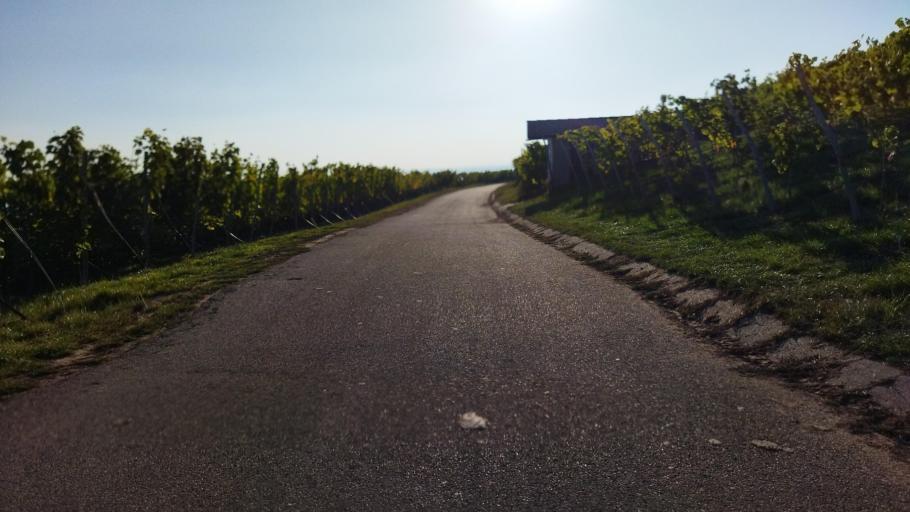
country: DE
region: Baden-Wuerttemberg
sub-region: Regierungsbezirk Stuttgart
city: Freudental
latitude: 49.0020
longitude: 9.0493
